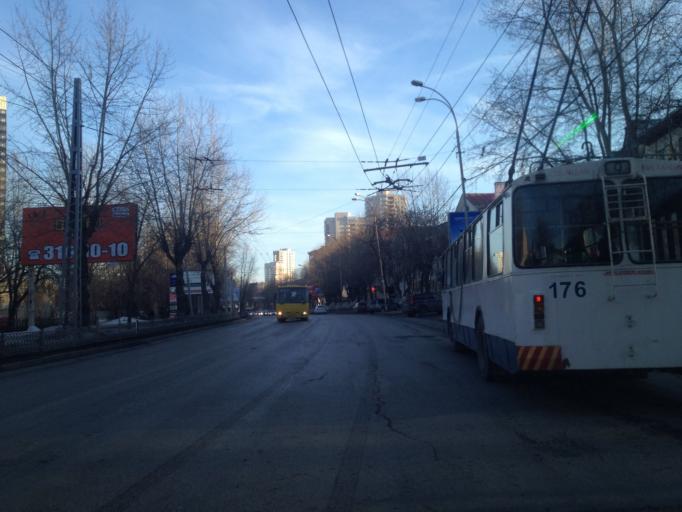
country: RU
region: Sverdlovsk
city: Yekaterinburg
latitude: 56.8073
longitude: 60.6242
